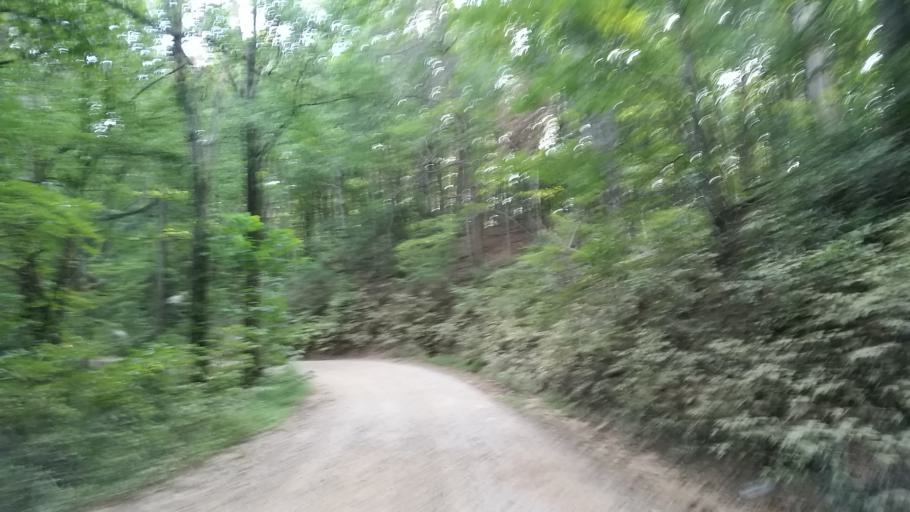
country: US
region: Georgia
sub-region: Lumpkin County
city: Dahlonega
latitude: 34.6357
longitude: -84.1004
